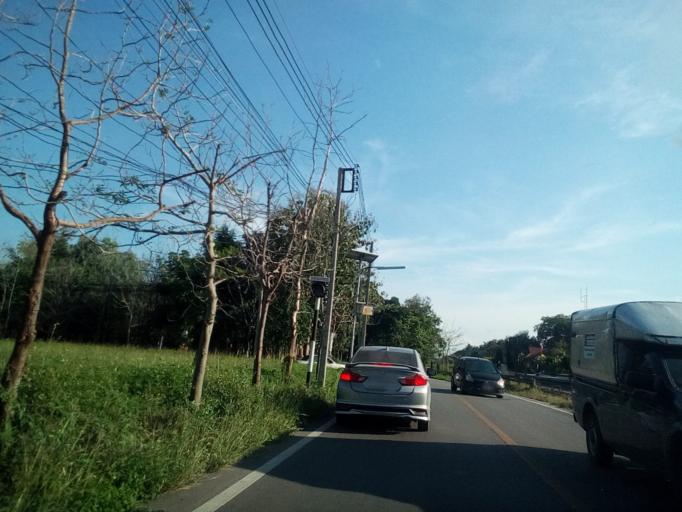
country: TH
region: Chiang Mai
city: Saraphi
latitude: 18.7114
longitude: 99.0415
